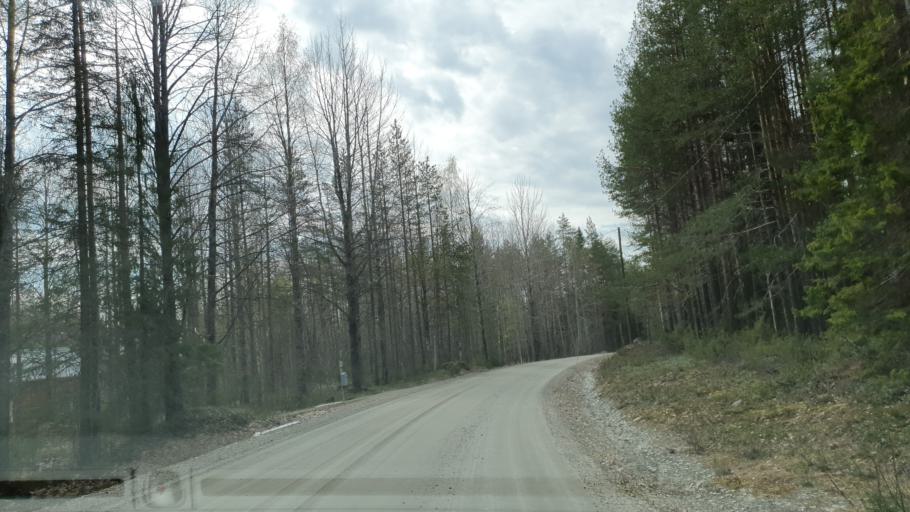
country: FI
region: Kainuu
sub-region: Kehys-Kainuu
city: Kuhmo
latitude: 64.0998
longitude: 29.9393
